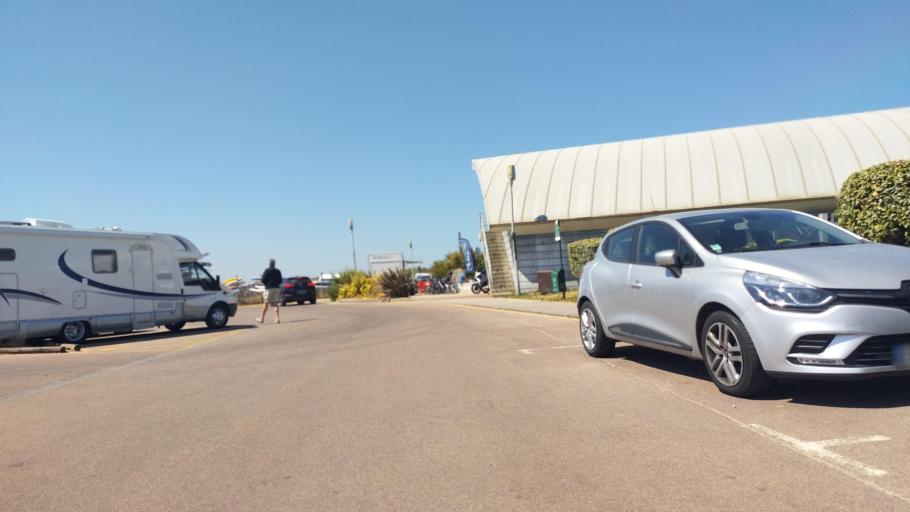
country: FR
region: Lower Normandy
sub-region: Departement du Calvados
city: Courseulles-sur-Mer
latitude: 49.3369
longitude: -0.4642
